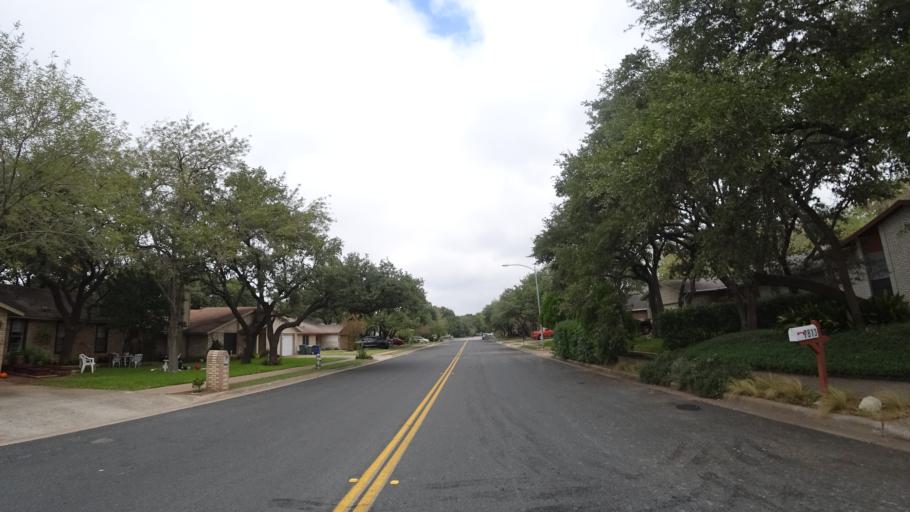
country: US
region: Texas
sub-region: Travis County
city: Shady Hollow
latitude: 30.2061
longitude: -97.8400
